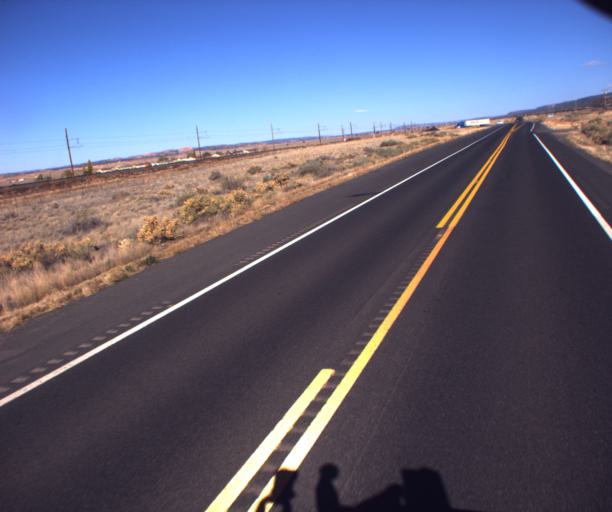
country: US
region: Arizona
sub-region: Coconino County
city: Kaibito
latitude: 36.4596
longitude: -110.6958
